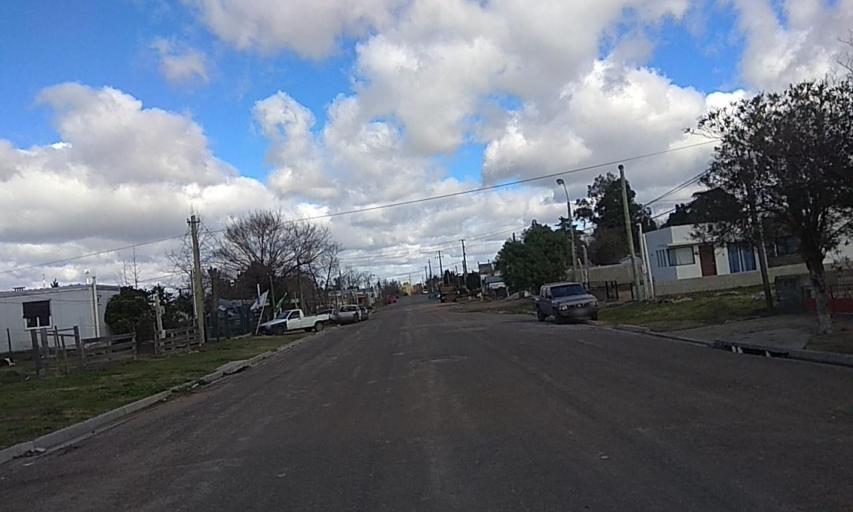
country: UY
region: Florida
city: Florida
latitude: -34.0837
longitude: -56.2180
